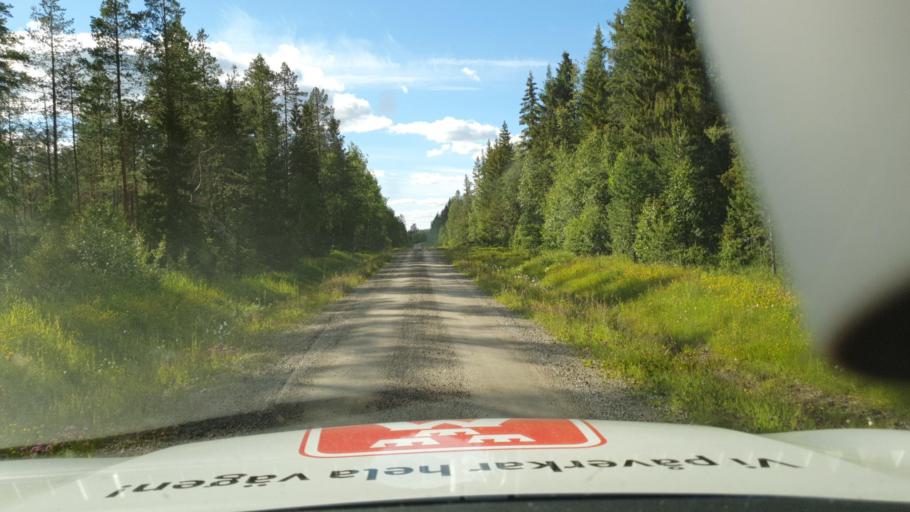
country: SE
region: Vaesterbotten
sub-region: Lycksele Kommun
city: Lycksele
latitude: 64.4688
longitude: 18.2932
